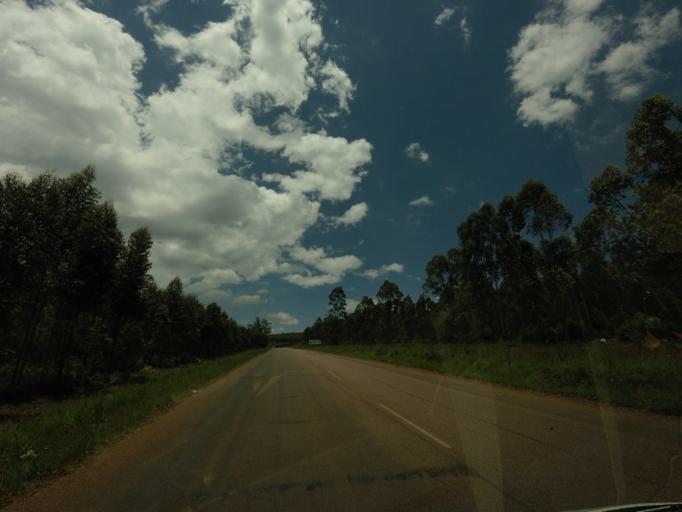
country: ZA
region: Mpumalanga
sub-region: Ehlanzeni District
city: Graksop
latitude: -25.0782
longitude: 30.7960
